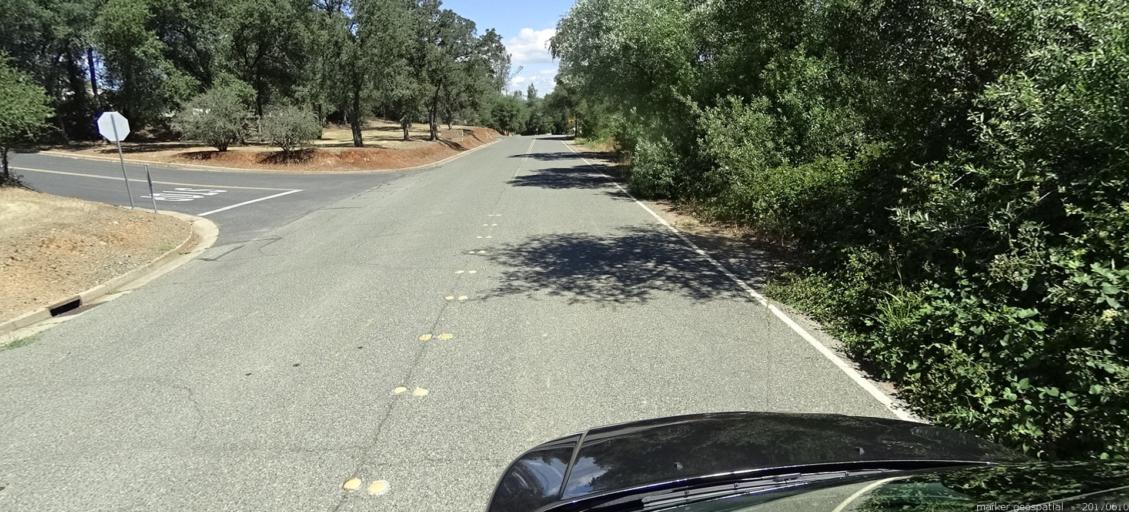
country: US
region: California
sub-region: Butte County
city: Oroville East
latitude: 39.5102
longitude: -121.5034
